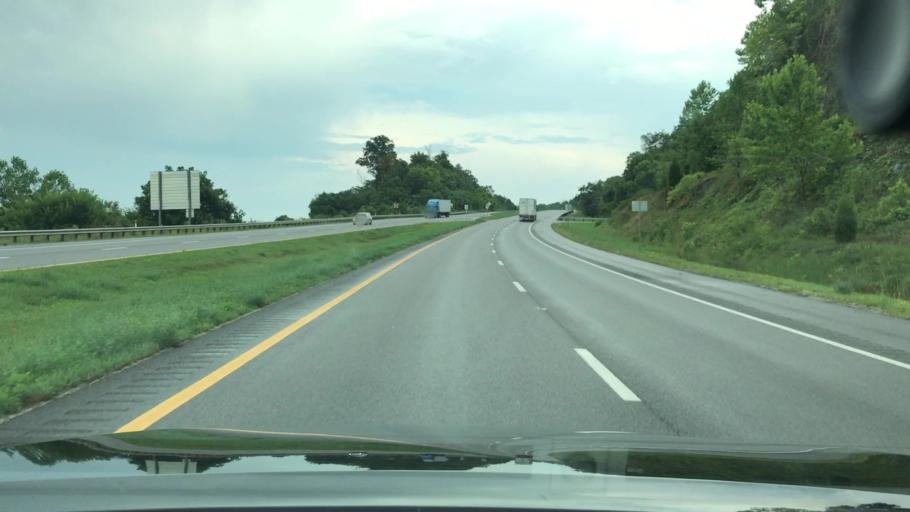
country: US
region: West Virginia
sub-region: Mason County
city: Point Pleasant
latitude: 38.8277
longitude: -82.1305
